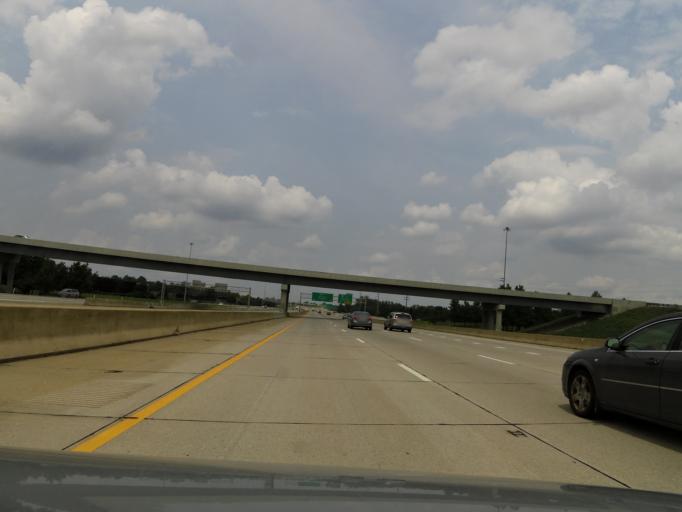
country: US
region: Kentucky
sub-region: Jefferson County
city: Saint Regis Park
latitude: 38.2387
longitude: -85.6229
